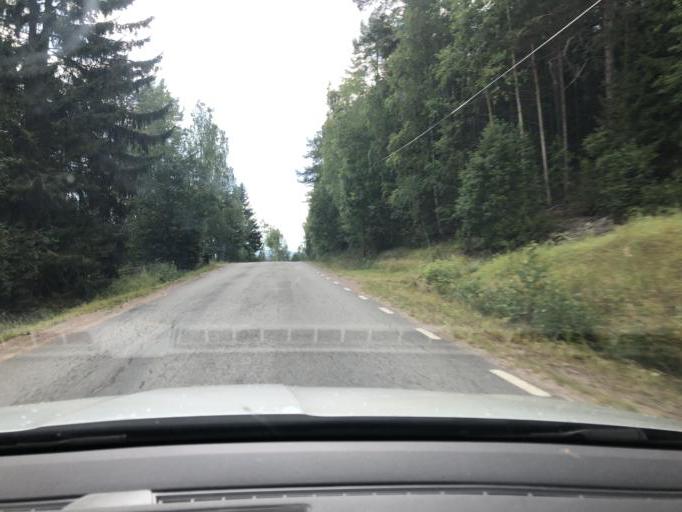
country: SE
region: Vaesternorrland
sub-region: Solleftea Kommun
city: Solleftea
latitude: 63.2072
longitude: 17.1566
